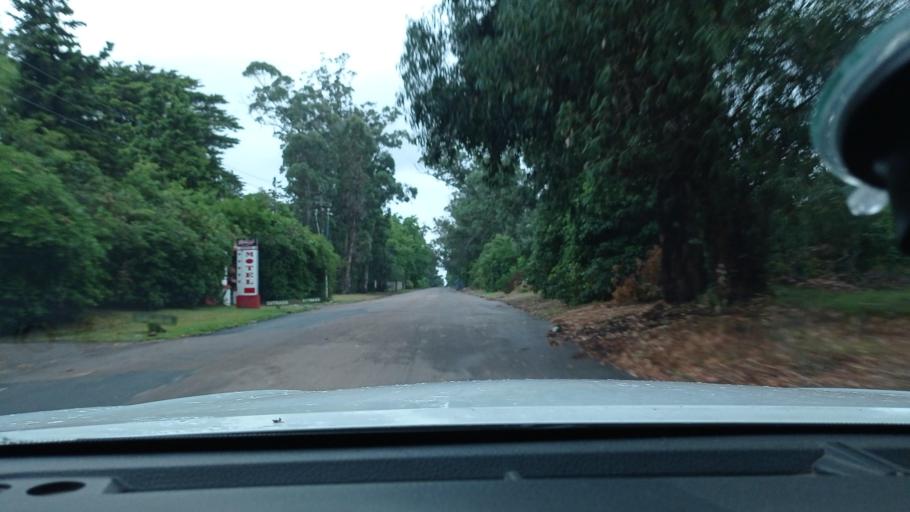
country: UY
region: Maldonado
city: Maldonado
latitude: -34.9165
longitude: -54.9116
